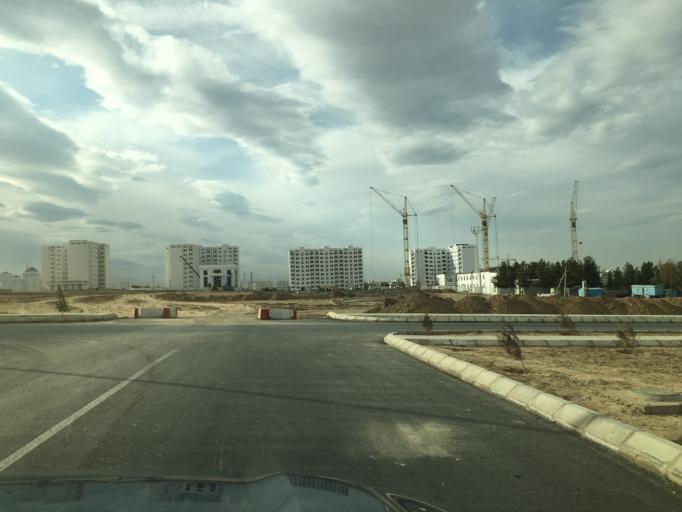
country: TM
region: Ahal
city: Ashgabat
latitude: 37.8987
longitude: 58.4115
